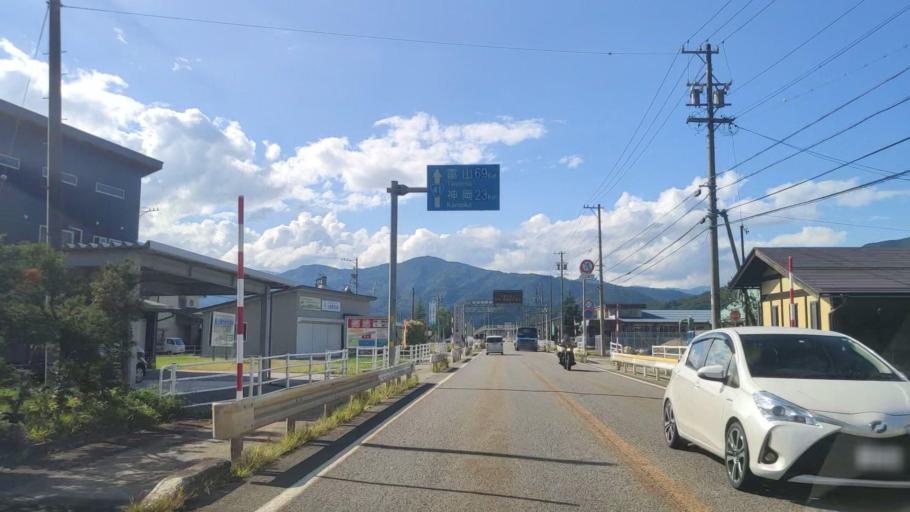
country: JP
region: Gifu
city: Takayama
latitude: 36.2537
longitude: 137.1609
